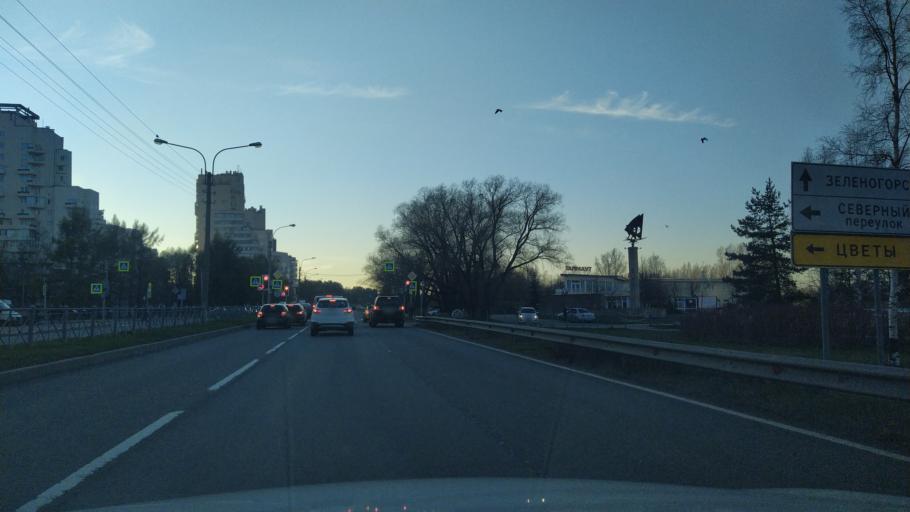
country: RU
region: St.-Petersburg
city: Sestroretsk
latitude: 60.1034
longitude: 29.9776
